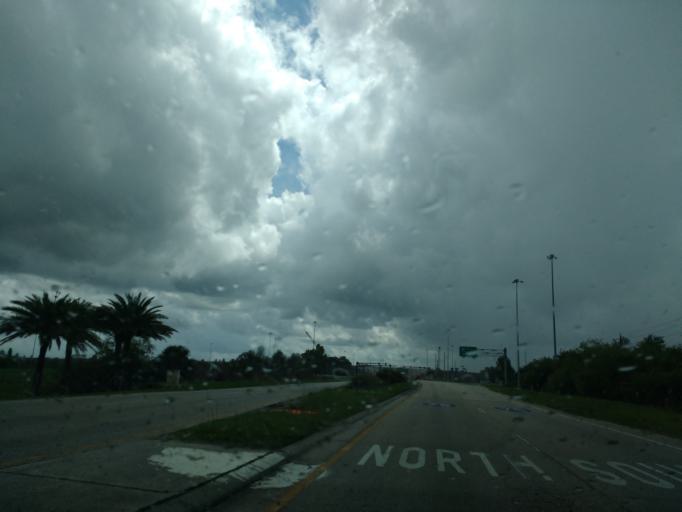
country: US
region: Florida
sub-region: Charlotte County
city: Charlotte Park
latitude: 26.8948
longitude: -82.0070
